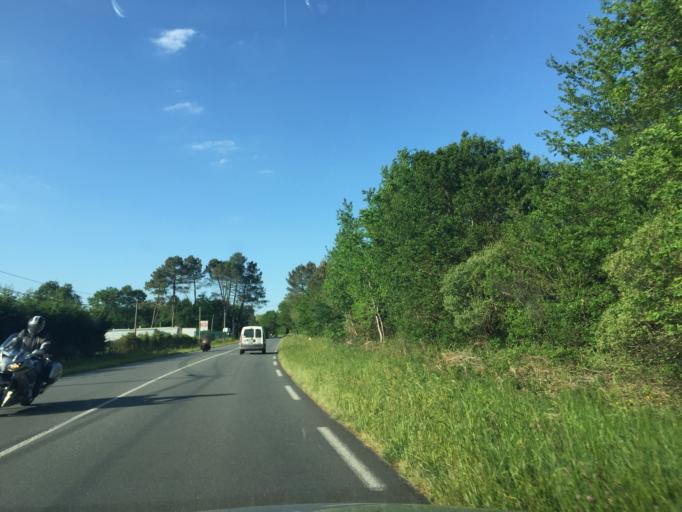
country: FR
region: Poitou-Charentes
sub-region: Departement de la Charente-Maritime
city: Saint-Aigulin
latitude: 45.1281
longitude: -0.0079
